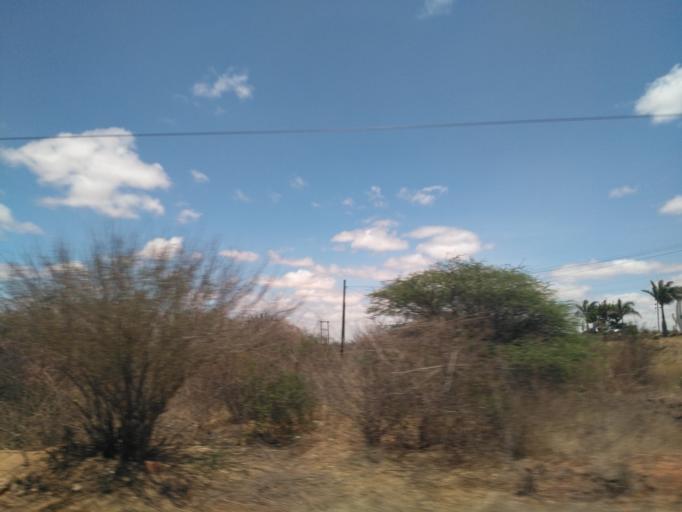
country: TZ
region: Dodoma
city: Kisasa
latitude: -6.2206
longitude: 35.8109
